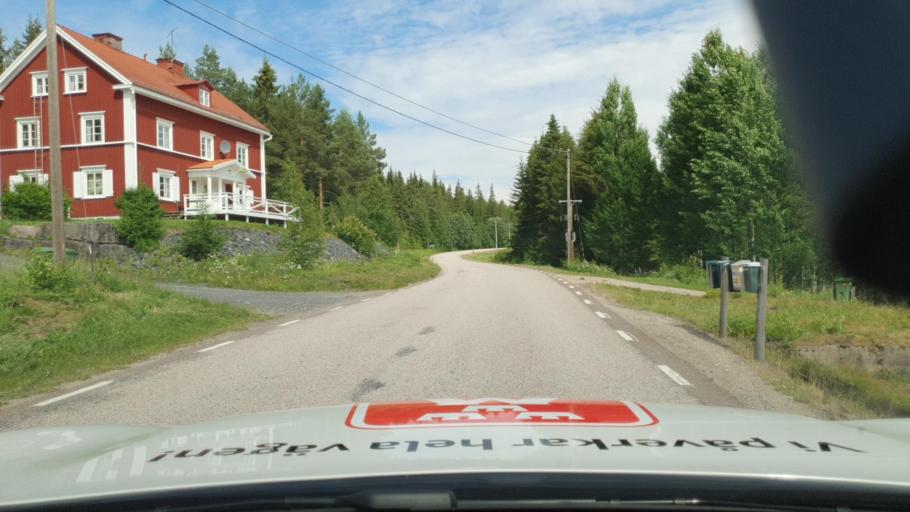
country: NO
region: Hedmark
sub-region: Asnes
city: Flisa
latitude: 60.6931
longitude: 12.4644
